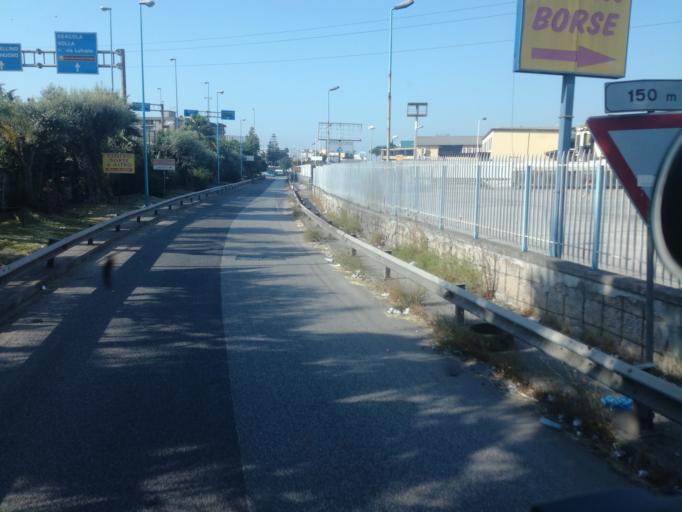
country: IT
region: Campania
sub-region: Provincia di Napoli
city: Arpino
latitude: 40.8934
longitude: 14.3242
